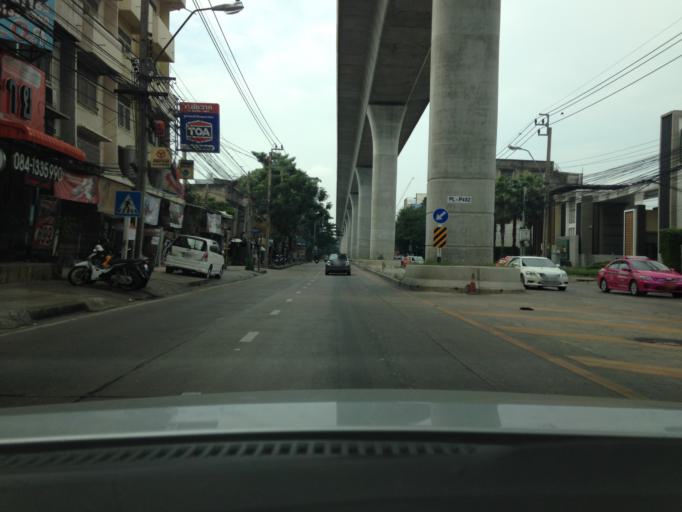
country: TH
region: Nonthaburi
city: Mueang Nonthaburi
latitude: 13.8349
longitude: 100.5204
